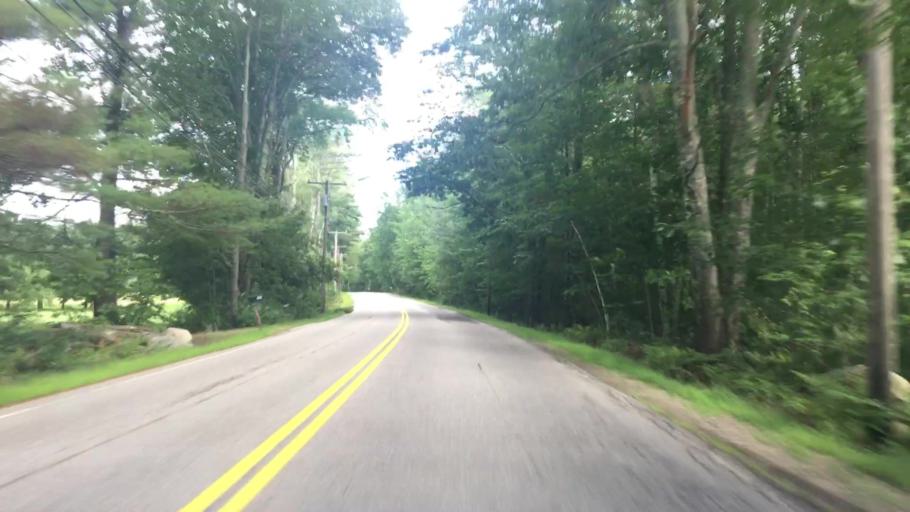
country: US
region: Maine
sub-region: York County
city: West Kennebunk
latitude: 43.4545
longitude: -70.6148
